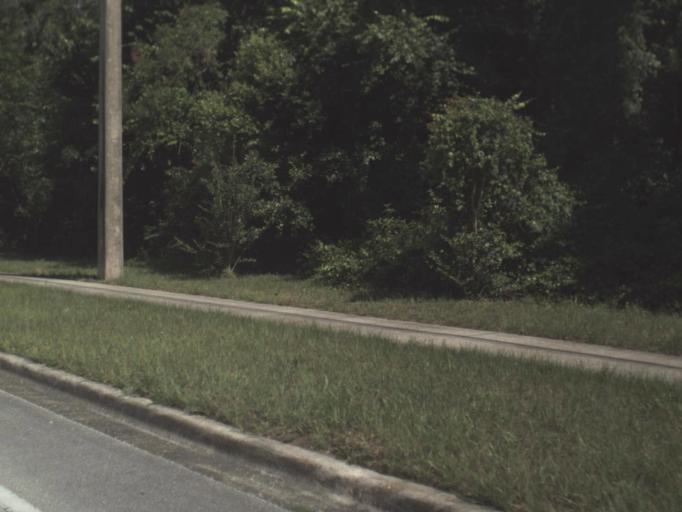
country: US
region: Florida
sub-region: Saint Johns County
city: Fruit Cove
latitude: 30.2153
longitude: -81.5361
